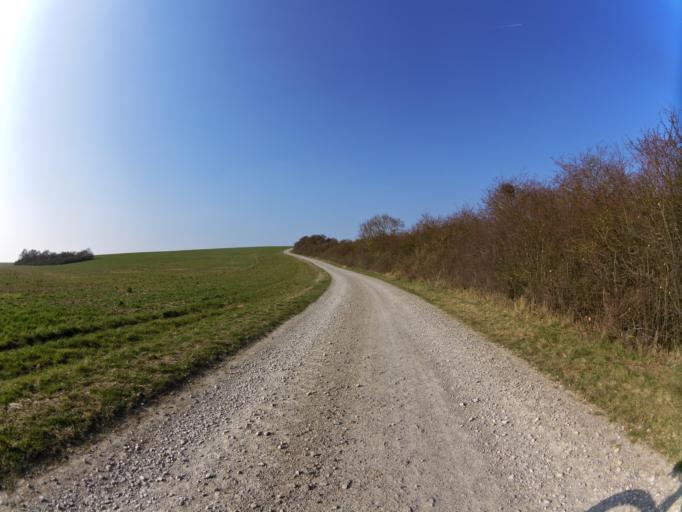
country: DE
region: Bavaria
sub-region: Regierungsbezirk Unterfranken
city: Winterhausen
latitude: 49.6790
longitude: 9.9908
